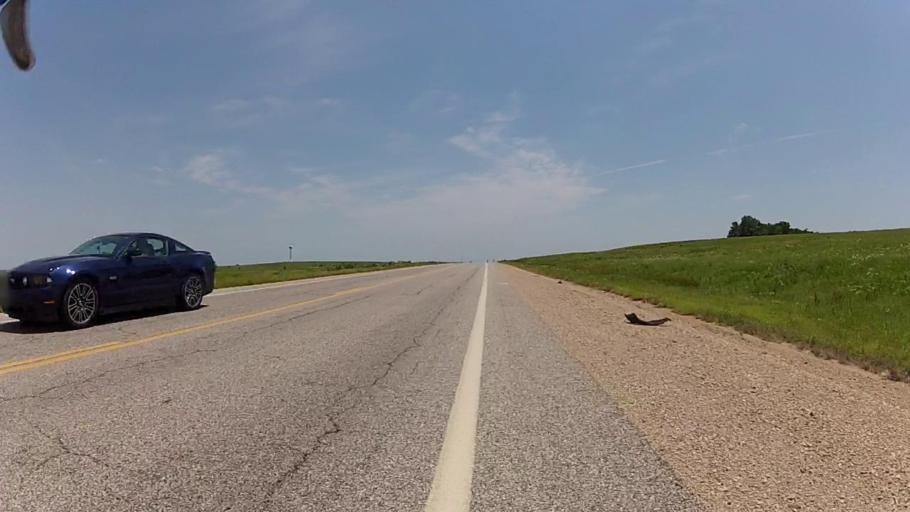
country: US
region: Kansas
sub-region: Chautauqua County
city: Sedan
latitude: 37.1106
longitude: -96.2554
